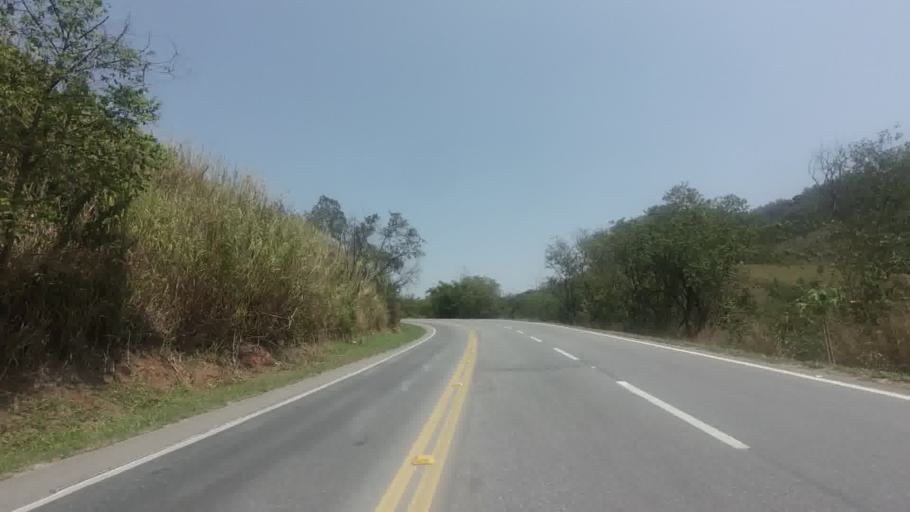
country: BR
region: Espirito Santo
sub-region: Rio Novo Do Sul
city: Rio Novo do Sul
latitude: -20.8832
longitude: -40.9796
